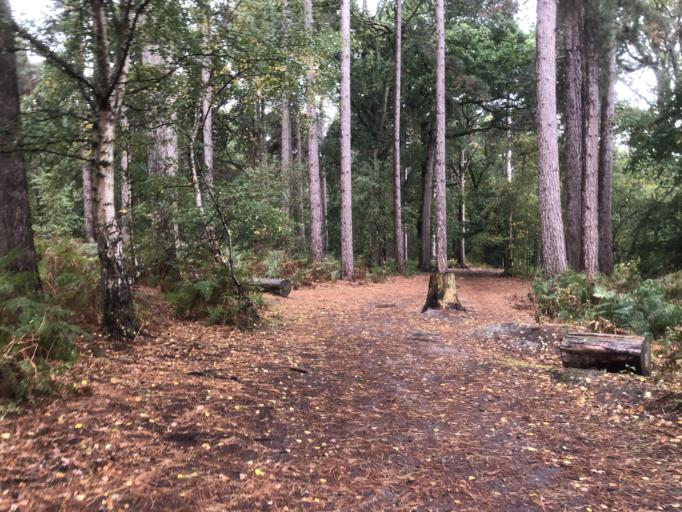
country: GB
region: England
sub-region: Norfolk
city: Spixworth
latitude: 52.6543
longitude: 1.3422
